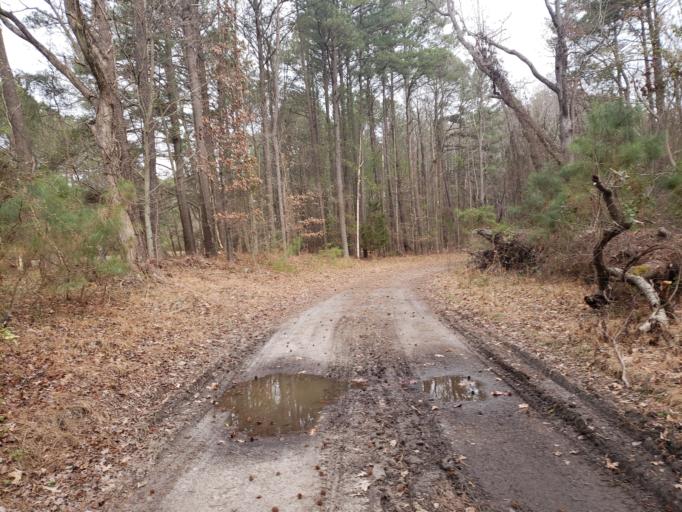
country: US
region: Virginia
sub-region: City of Newport News
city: Newport News
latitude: 36.8974
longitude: -76.4331
